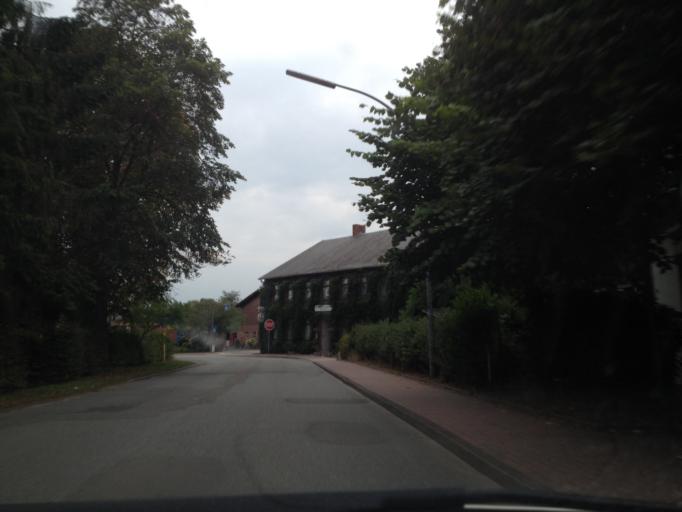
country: DE
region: Schleswig-Holstein
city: Rickling
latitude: 53.9997
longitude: 10.1707
